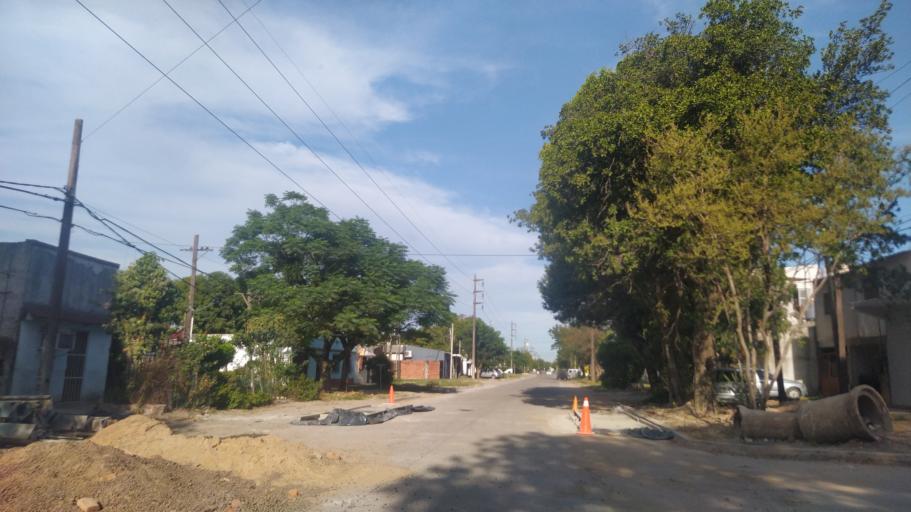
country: AR
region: Corrientes
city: Corrientes
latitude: -27.4819
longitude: -58.8043
